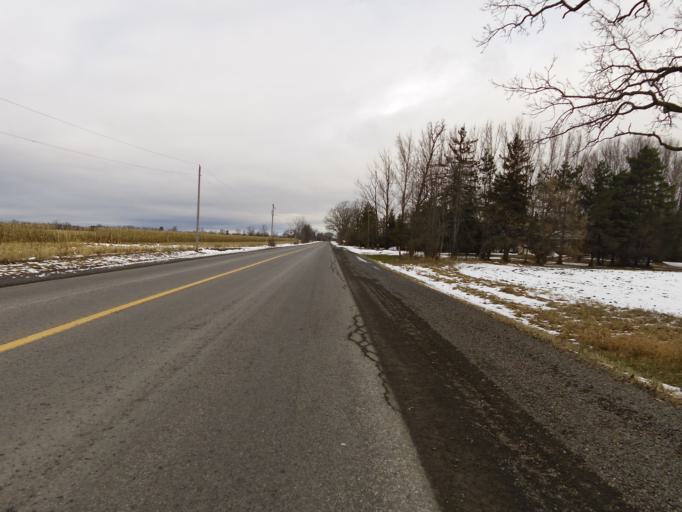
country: CA
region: Ontario
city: Carleton Place
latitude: 45.3396
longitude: -76.0759
